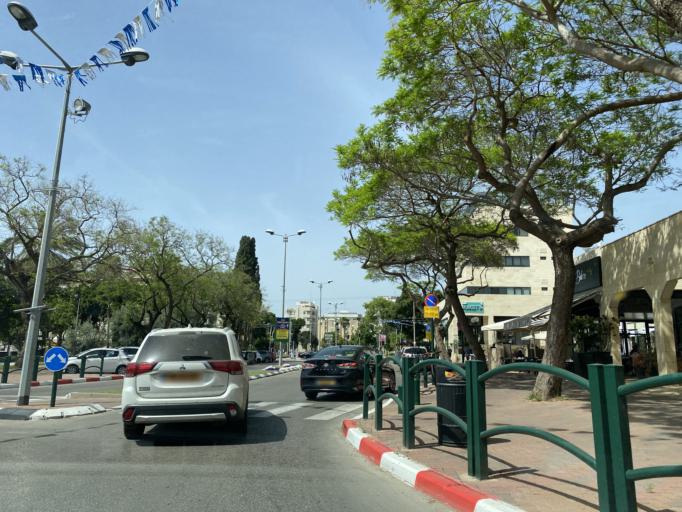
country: IL
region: Central District
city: Ra'anana
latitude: 32.1801
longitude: 34.8719
